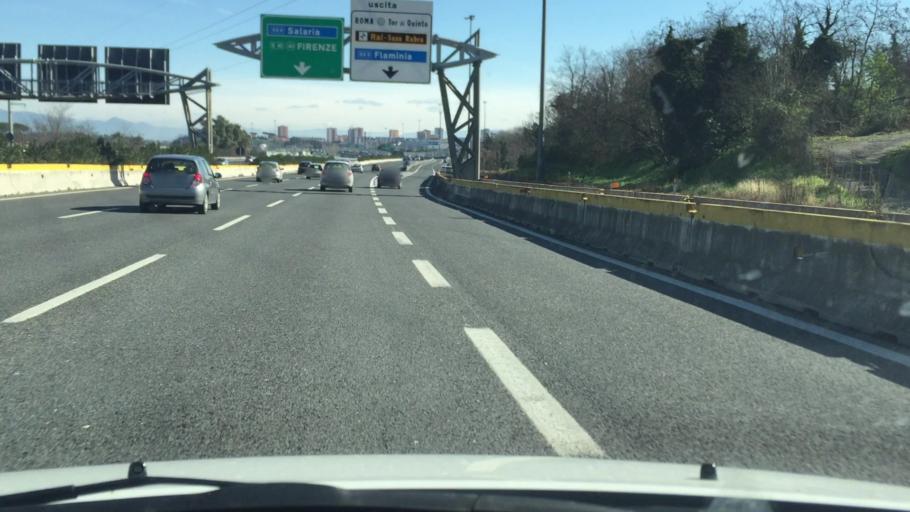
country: IT
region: Latium
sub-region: Citta metropolitana di Roma Capitale
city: Monte Caminetto
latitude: 41.9863
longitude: 12.4817
